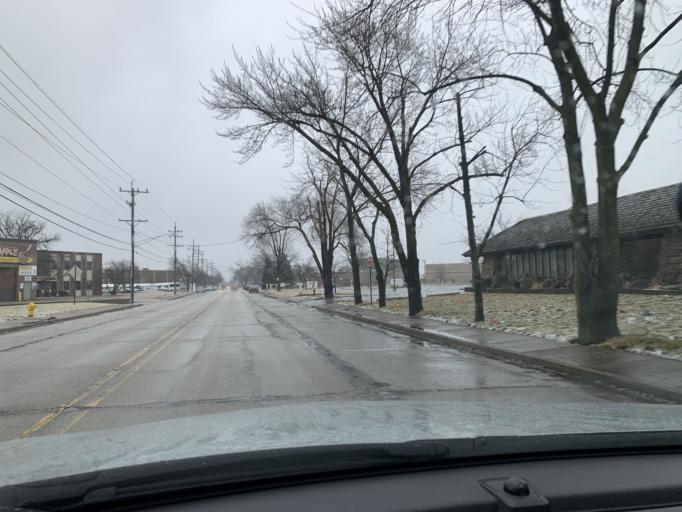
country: US
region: Illinois
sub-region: Cook County
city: Niles
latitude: 42.0152
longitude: -87.7845
